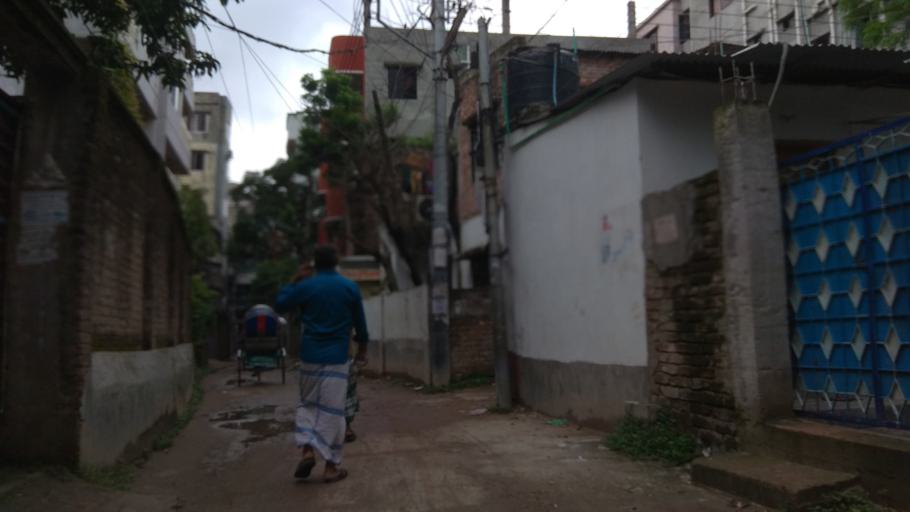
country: BD
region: Dhaka
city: Azimpur
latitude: 23.7988
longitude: 90.3675
